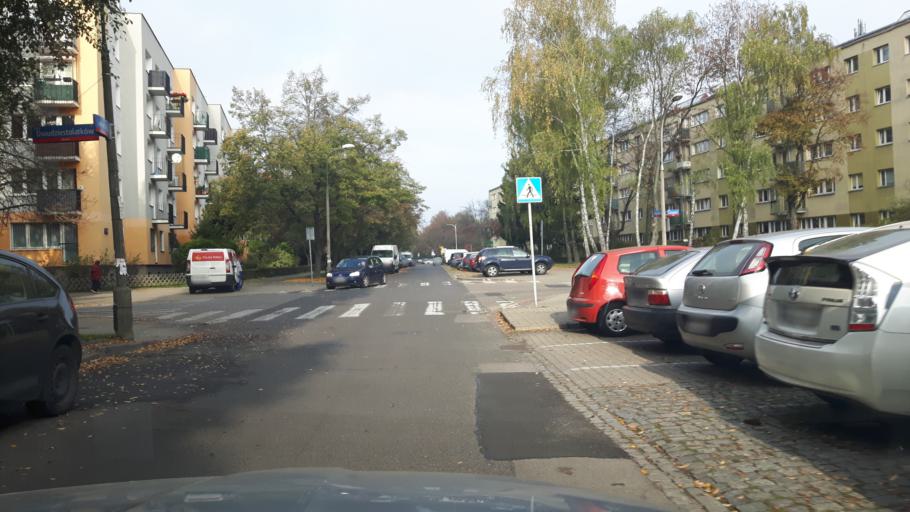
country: PL
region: Masovian Voivodeship
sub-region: Warszawa
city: Wlochy
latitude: 52.1920
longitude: 20.9709
